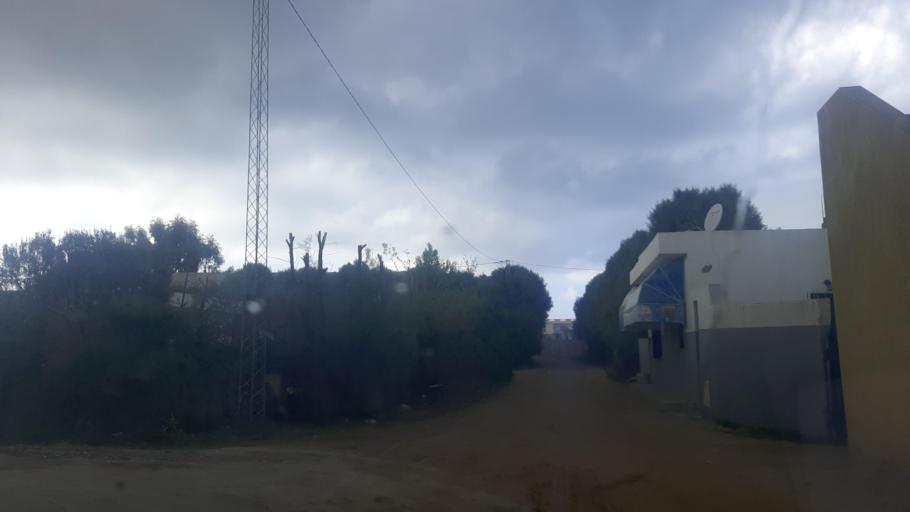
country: TN
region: Nabul
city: Manzil Bu Zalafah
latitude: 36.7367
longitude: 10.5246
